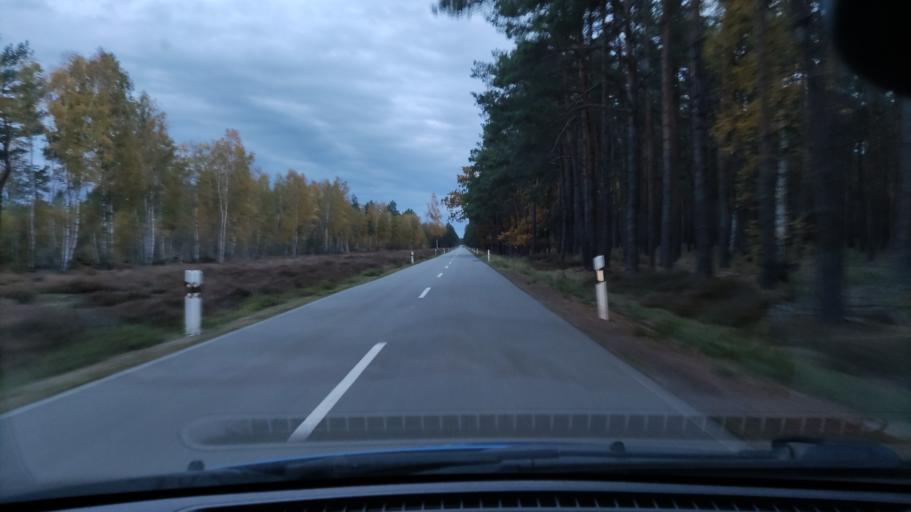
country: DE
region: Lower Saxony
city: Prezelle
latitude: 52.9727
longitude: 11.3989
